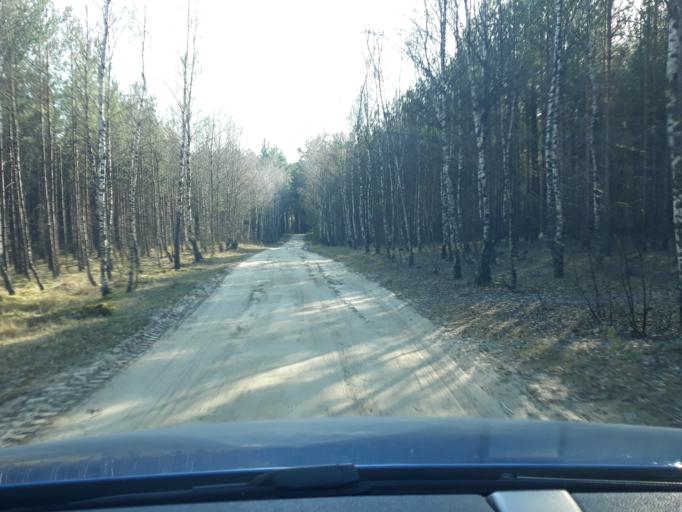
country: PL
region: Pomeranian Voivodeship
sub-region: Powiat bytowski
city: Lipnica
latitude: 53.8875
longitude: 17.4897
